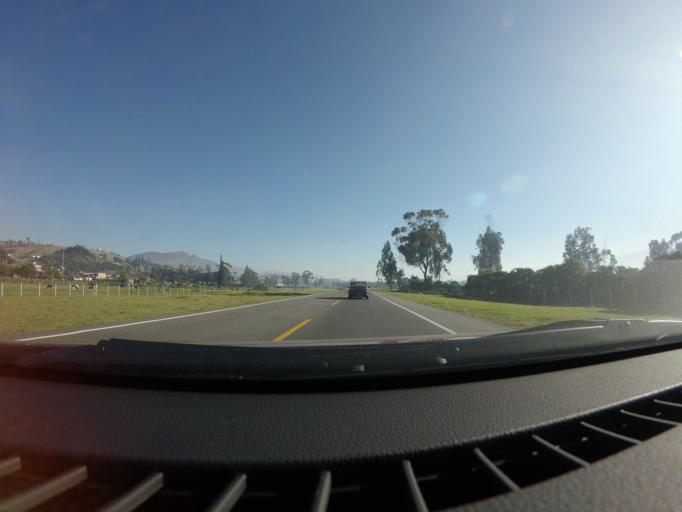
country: CO
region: Cundinamarca
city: Cogua
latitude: 5.0535
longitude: -73.9579
